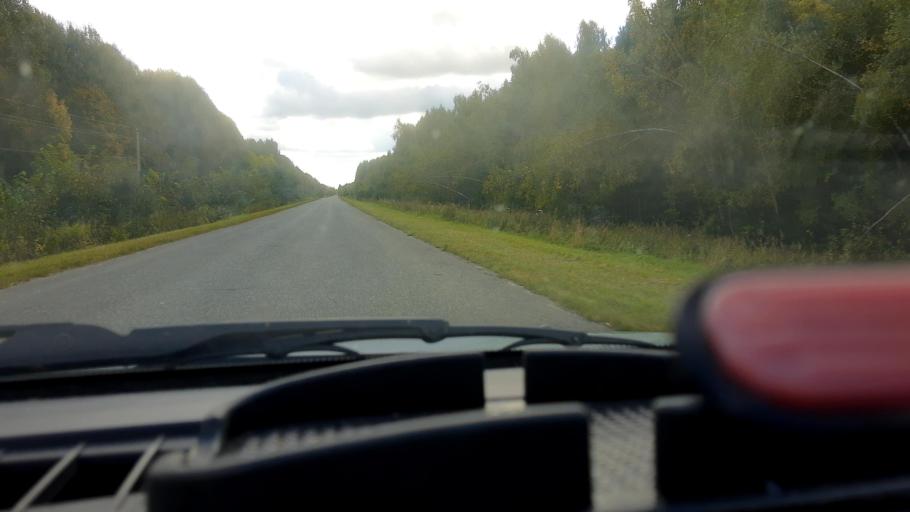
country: RU
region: Mariy-El
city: Kilemary
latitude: 56.9176
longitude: 46.7200
